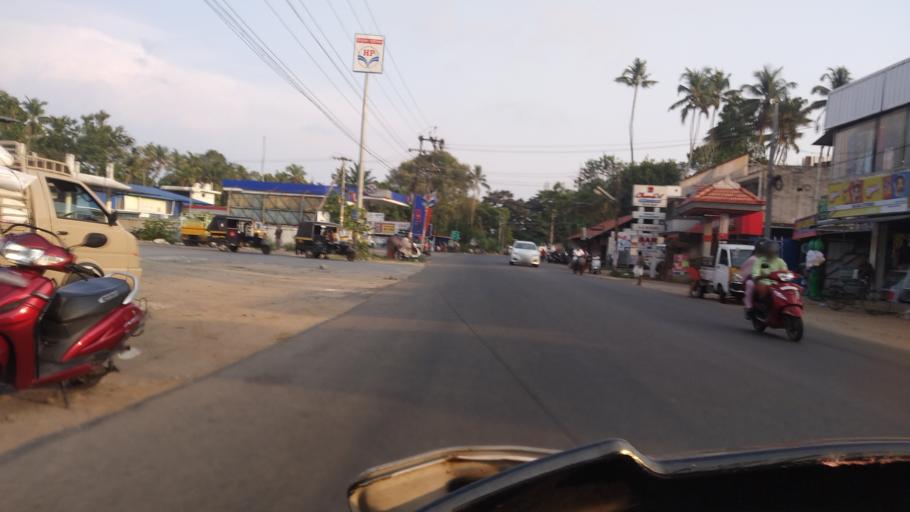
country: IN
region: Kerala
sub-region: Thrissur District
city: Irinjalakuda
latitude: 10.3233
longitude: 76.1445
